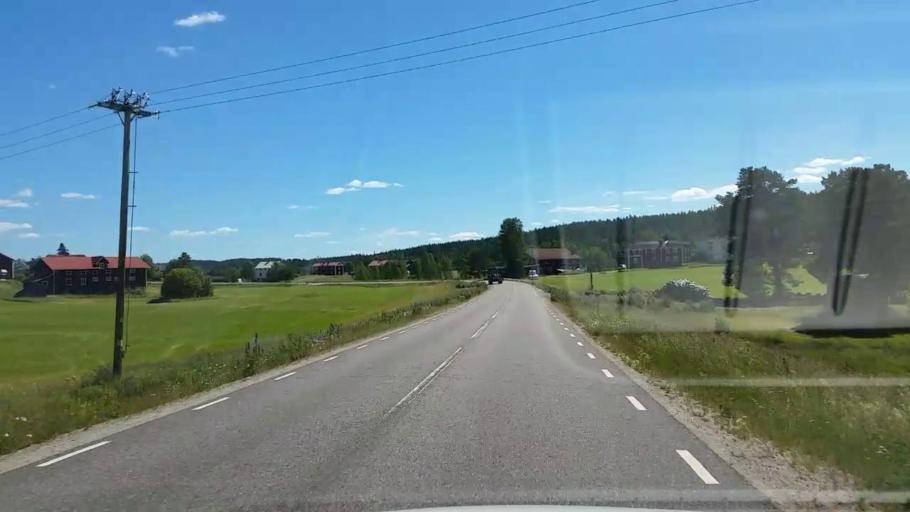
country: SE
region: Gaevleborg
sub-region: Ovanakers Kommun
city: Edsbyn
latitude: 61.4223
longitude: 15.7342
